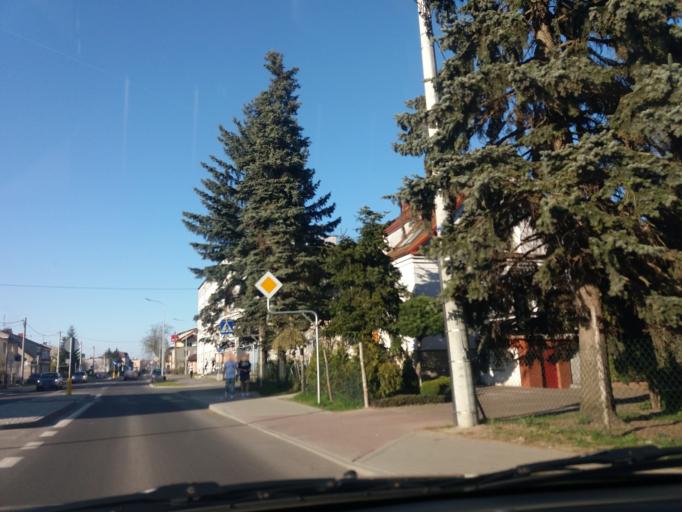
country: PL
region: Warmian-Masurian Voivodeship
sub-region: Powiat nidzicki
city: Nidzica
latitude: 53.3635
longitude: 20.4270
